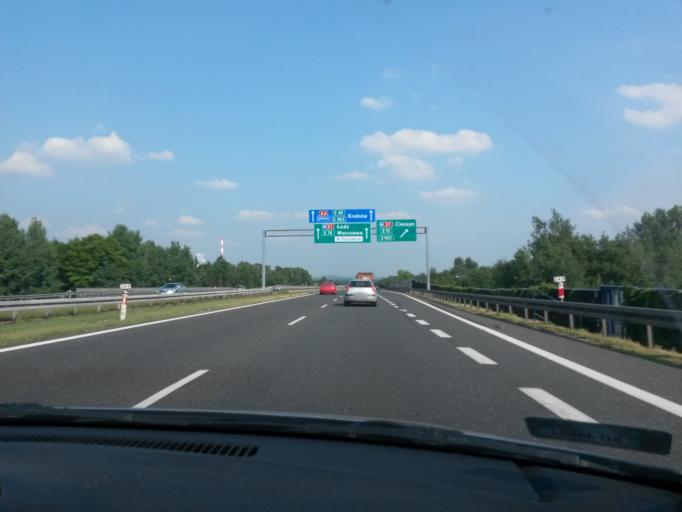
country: PL
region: Silesian Voivodeship
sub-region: Myslowice
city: Myslowice
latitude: 50.2100
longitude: 19.1563
